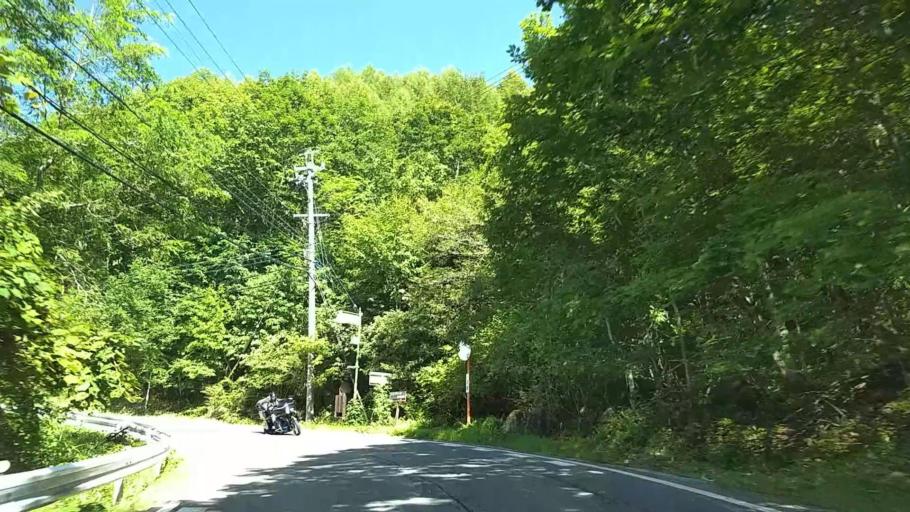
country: JP
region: Nagano
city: Chino
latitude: 36.0675
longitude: 138.2921
